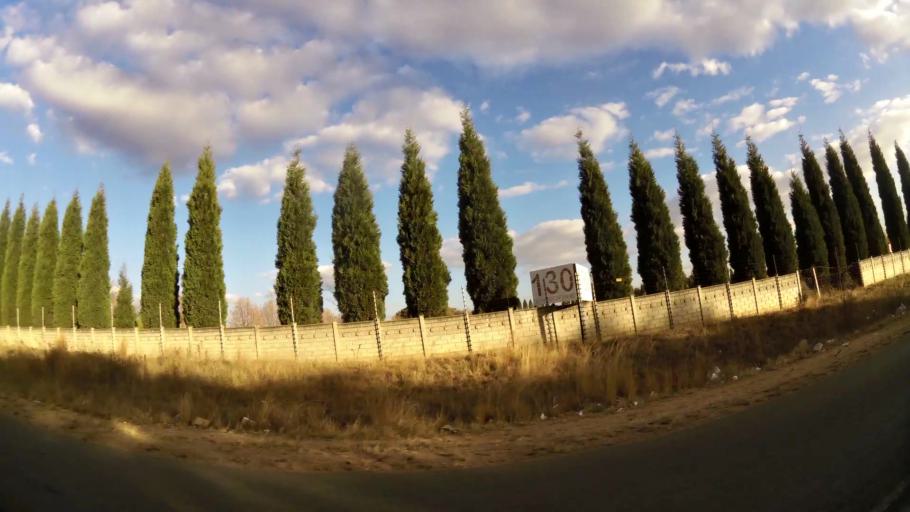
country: ZA
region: Gauteng
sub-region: City of Johannesburg Metropolitan Municipality
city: Midrand
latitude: -25.9571
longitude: 28.1680
